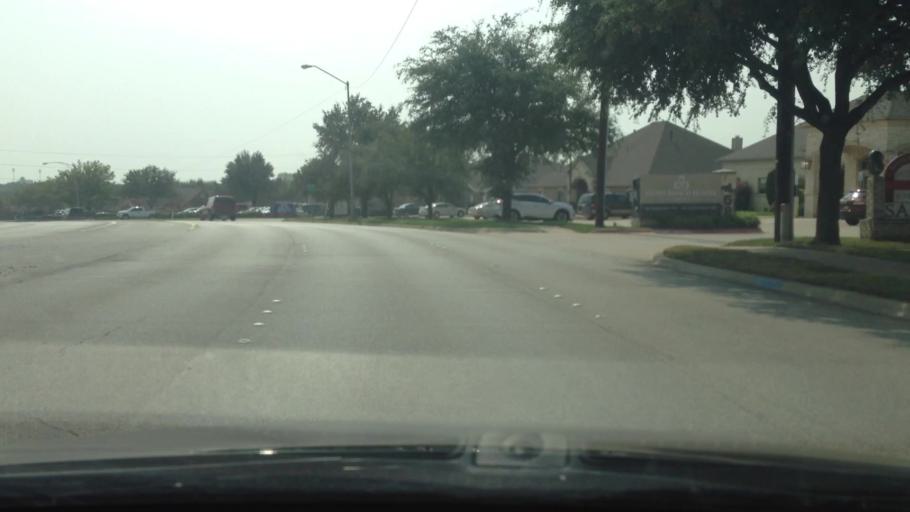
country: US
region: Texas
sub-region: Tarrant County
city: Colleyville
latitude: 32.8676
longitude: -97.1729
